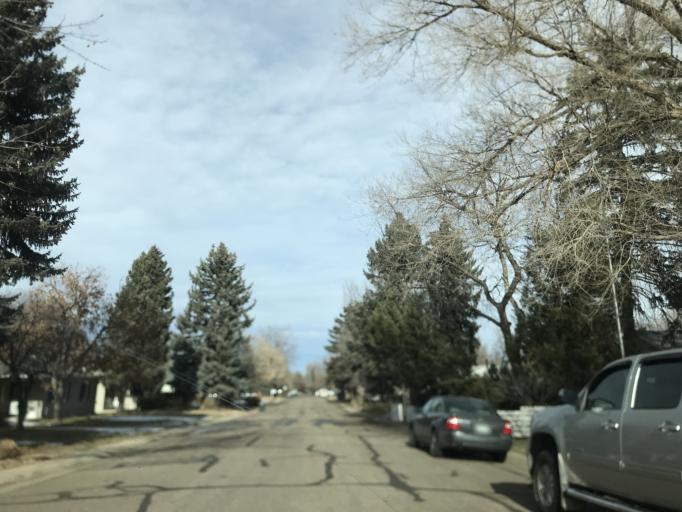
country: US
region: Colorado
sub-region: Arapahoe County
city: Littleton
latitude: 39.6008
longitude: -105.0105
